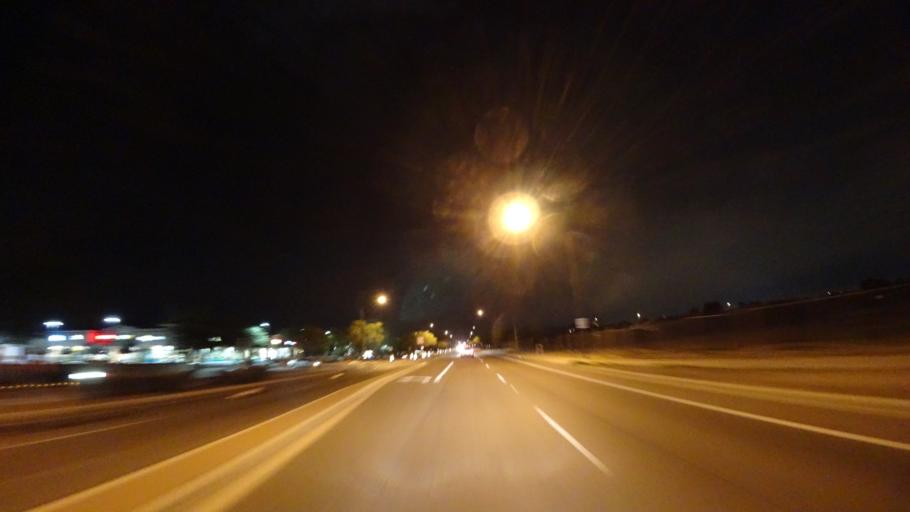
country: US
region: Arizona
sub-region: Maricopa County
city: Chandler
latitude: 33.2632
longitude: -111.7563
